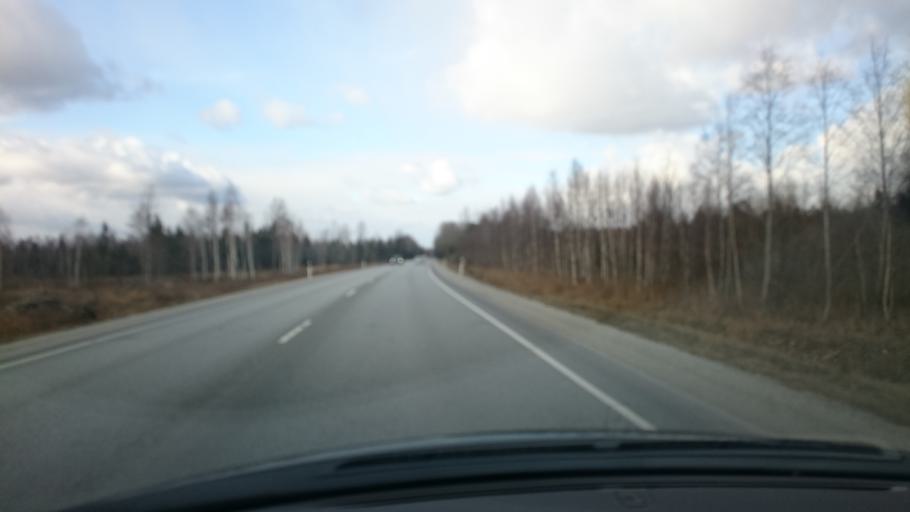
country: EE
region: Harju
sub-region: Nissi vald
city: Riisipere
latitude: 59.1607
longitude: 24.3437
